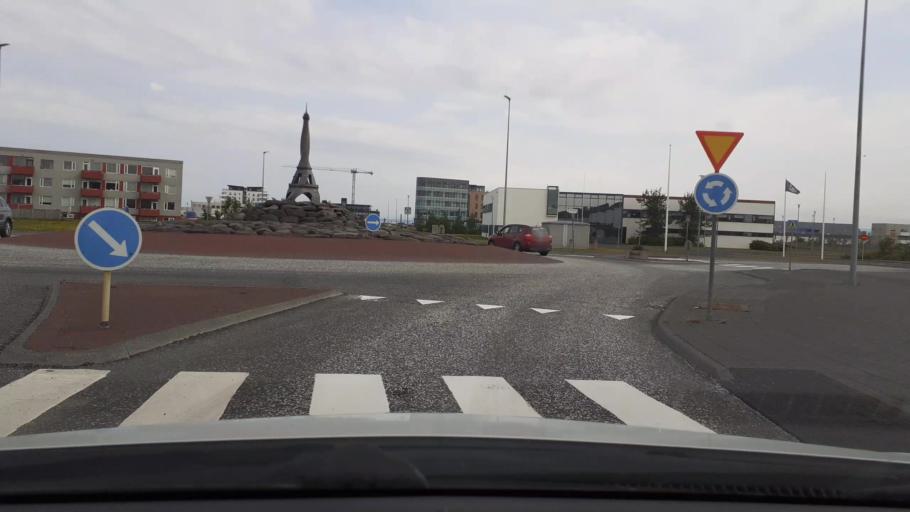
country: IS
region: Southern Peninsula
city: Reykjanesbaer
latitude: 63.9948
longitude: -22.5573
